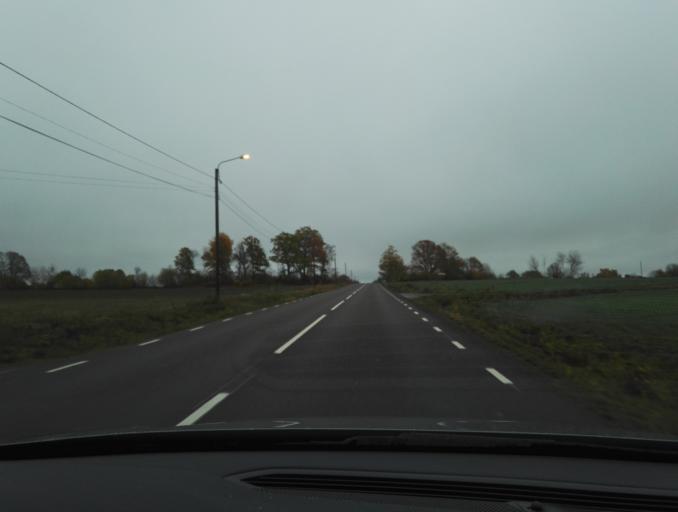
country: SE
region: Kronoberg
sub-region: Vaxjo Kommun
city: Rottne
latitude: 57.0240
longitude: 14.8389
